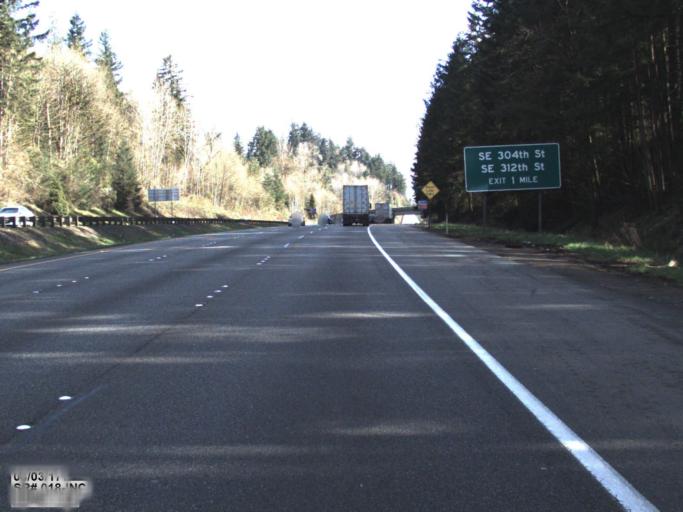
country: US
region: Washington
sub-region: King County
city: Lea Hill
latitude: 47.3161
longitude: -122.1677
